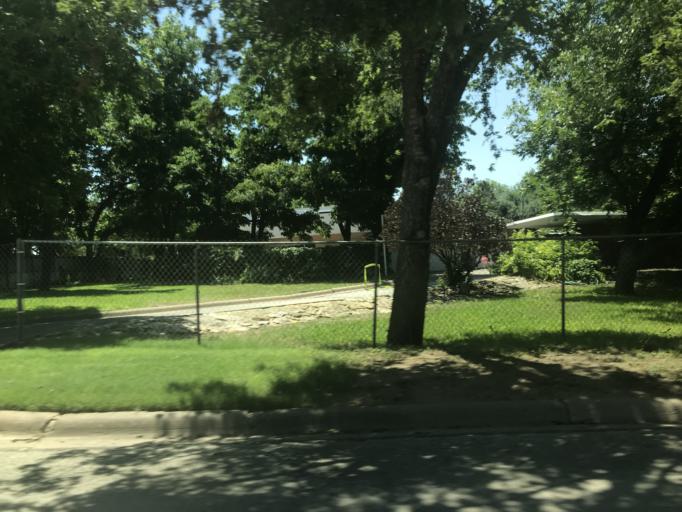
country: US
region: Texas
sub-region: Taylor County
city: Abilene
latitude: 32.4619
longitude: -99.7123
